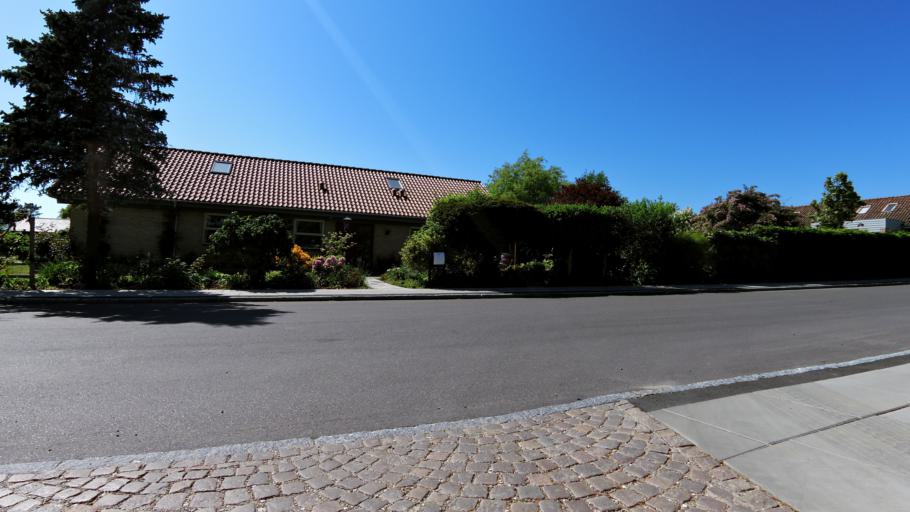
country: DK
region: Central Jutland
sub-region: Arhus Kommune
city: Framlev
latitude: 56.1419
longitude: 9.9969
